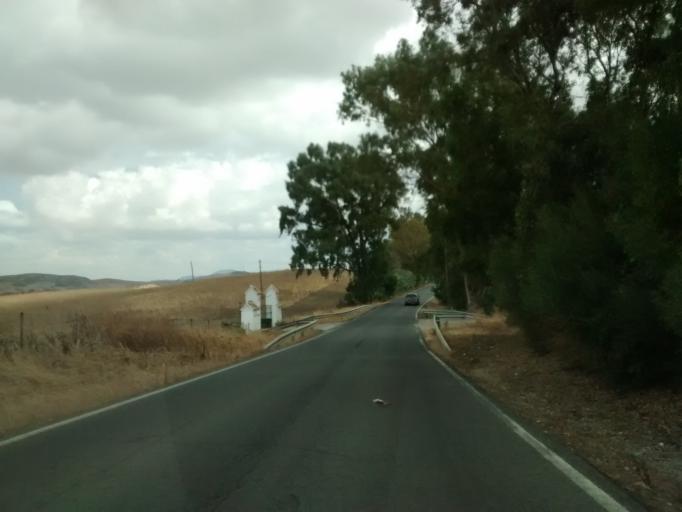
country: ES
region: Andalusia
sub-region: Provincia de Cadiz
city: Paterna de Rivera
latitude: 36.4978
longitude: -5.8890
